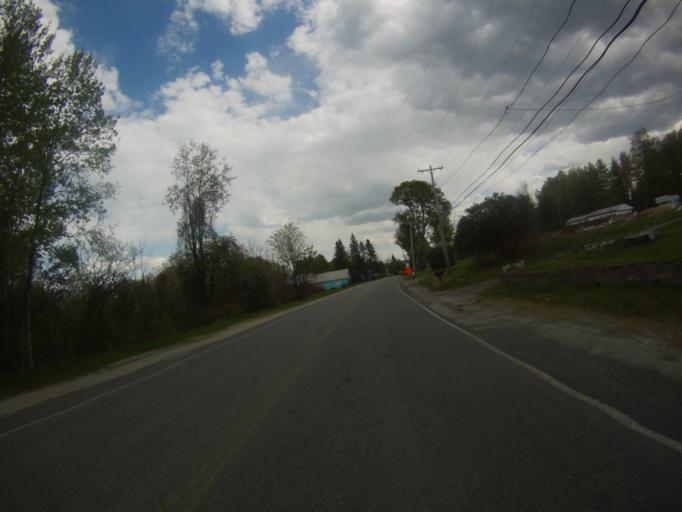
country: US
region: New York
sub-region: Essex County
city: Mineville
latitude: 44.0829
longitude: -73.5292
